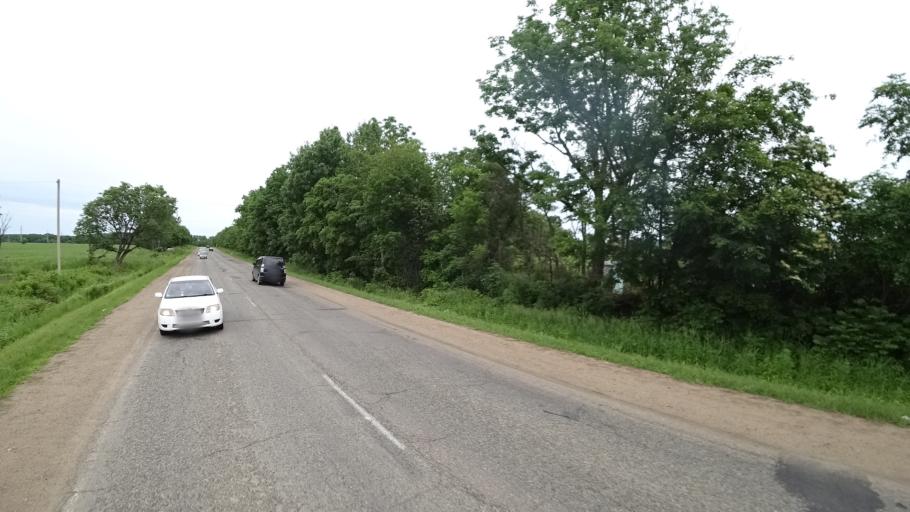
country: RU
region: Primorskiy
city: Novosysoyevka
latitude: 44.1838
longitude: 133.3515
